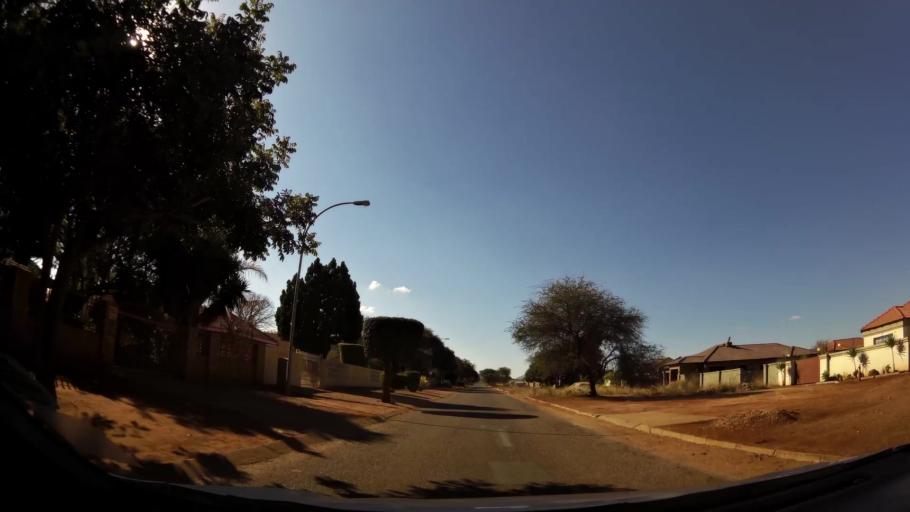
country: ZA
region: Limpopo
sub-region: Waterberg District Municipality
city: Mokopane
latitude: -24.2011
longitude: 28.9931
